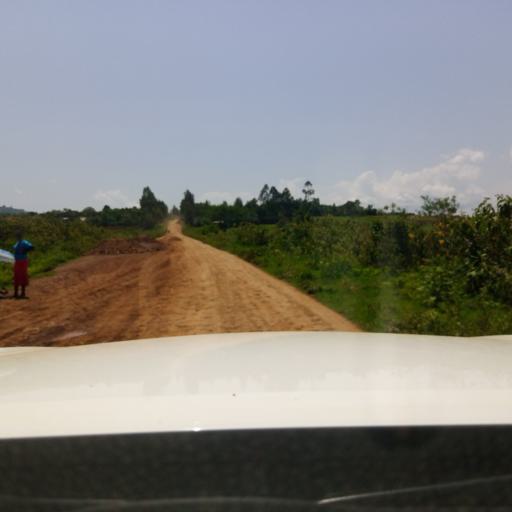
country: ET
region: Oromiya
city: Agaro
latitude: 8.1063
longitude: 36.9296
